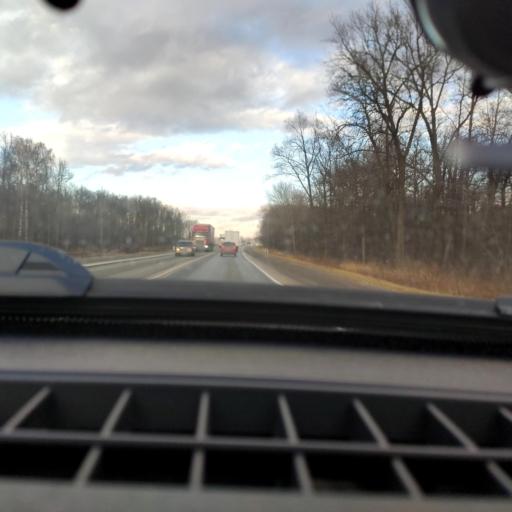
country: RU
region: Bashkortostan
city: Iglino
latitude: 54.7232
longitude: 56.2425
